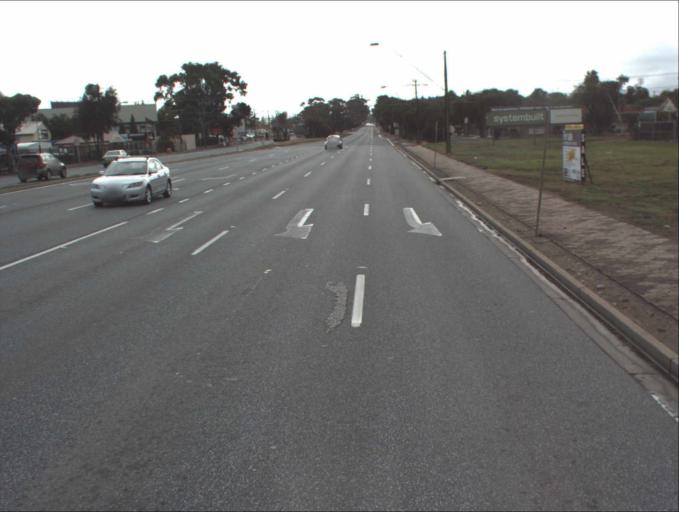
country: AU
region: South Australia
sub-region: Port Adelaide Enfield
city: Enfield
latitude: -34.8475
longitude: 138.6008
